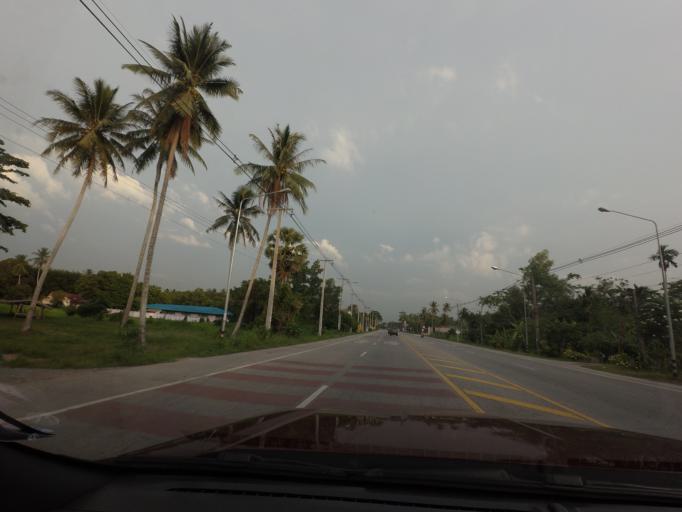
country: TH
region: Pattani
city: Mae Lan
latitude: 6.6222
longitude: 101.1886
